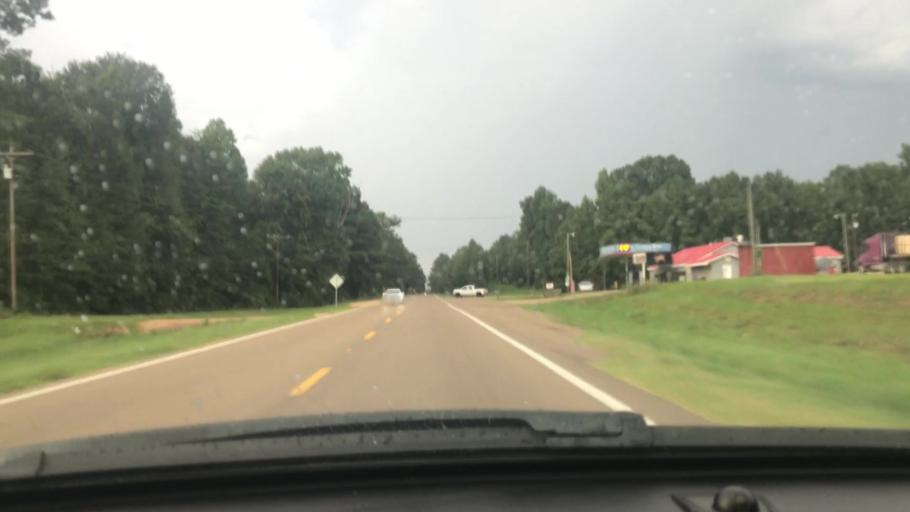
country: US
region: Mississippi
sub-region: Pike County
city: Summit
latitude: 31.3523
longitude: -90.6057
